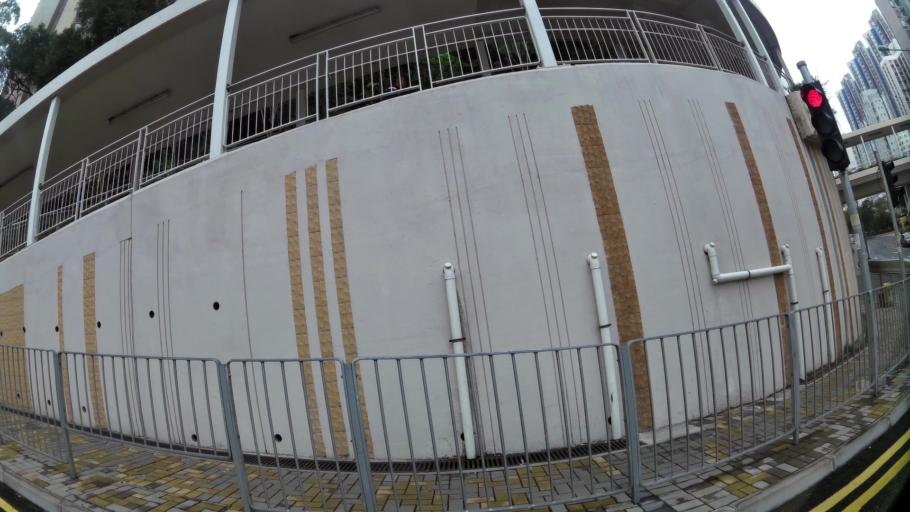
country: HK
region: Central and Western
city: Central
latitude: 22.2436
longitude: 114.1574
